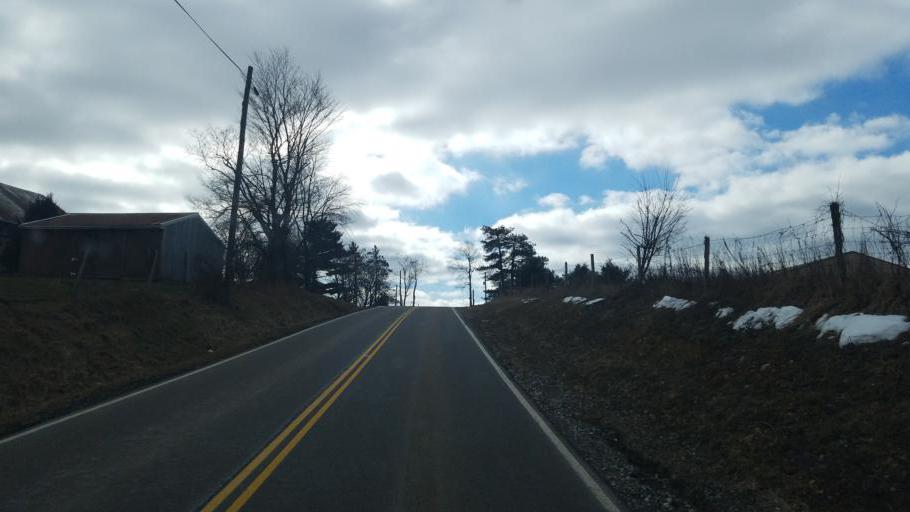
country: US
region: Ohio
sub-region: Knox County
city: Fredericktown
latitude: 40.5289
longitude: -82.5044
